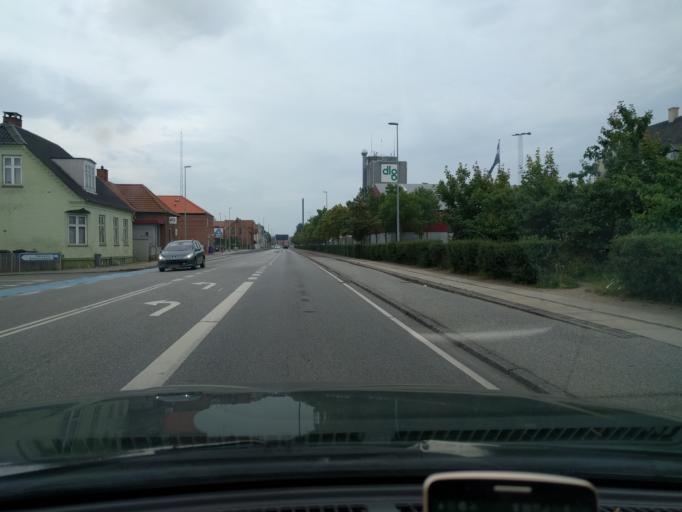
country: DK
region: Zealand
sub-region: Slagelse Kommune
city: Korsor
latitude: 55.3354
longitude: 11.1406
